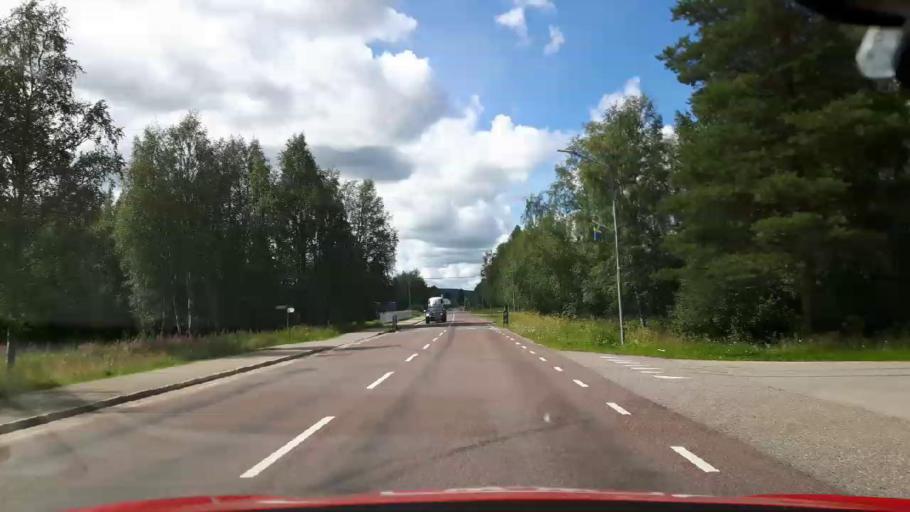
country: SE
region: Jaemtland
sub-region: Harjedalens Kommun
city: Sveg
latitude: 61.8541
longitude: 14.0846
